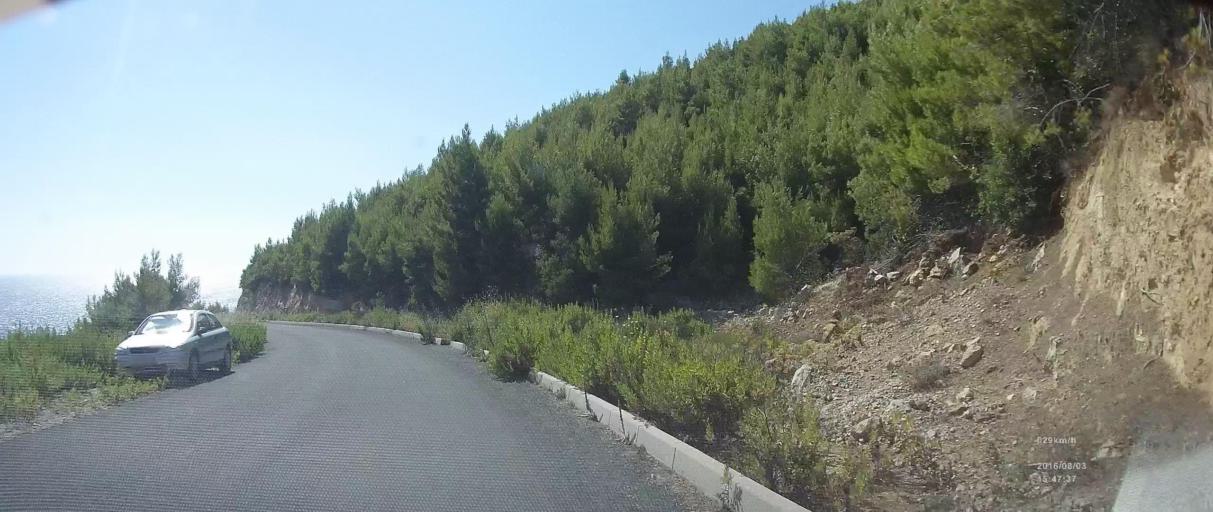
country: HR
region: Dubrovacko-Neretvanska
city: Blato
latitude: 42.7356
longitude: 17.5077
